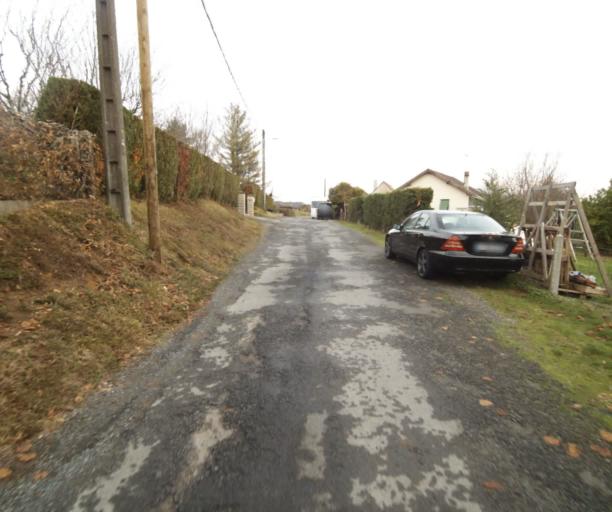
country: FR
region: Limousin
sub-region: Departement de la Correze
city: Chameyrat
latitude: 45.2686
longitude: 1.7024
